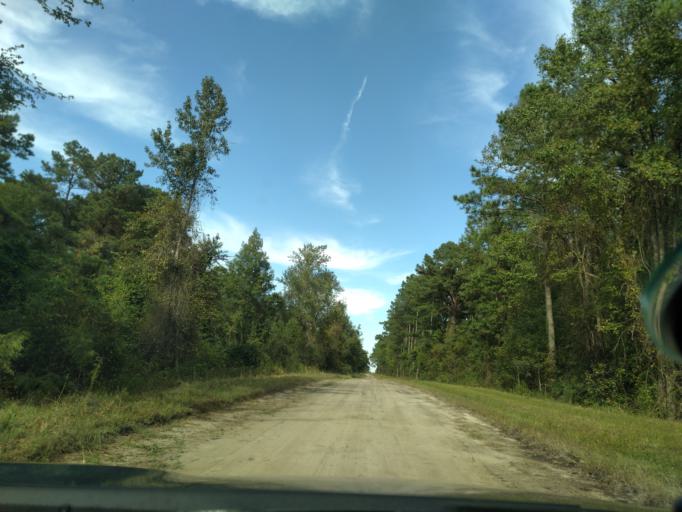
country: US
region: North Carolina
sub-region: Beaufort County
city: Belhaven
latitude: 35.7253
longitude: -76.5774
